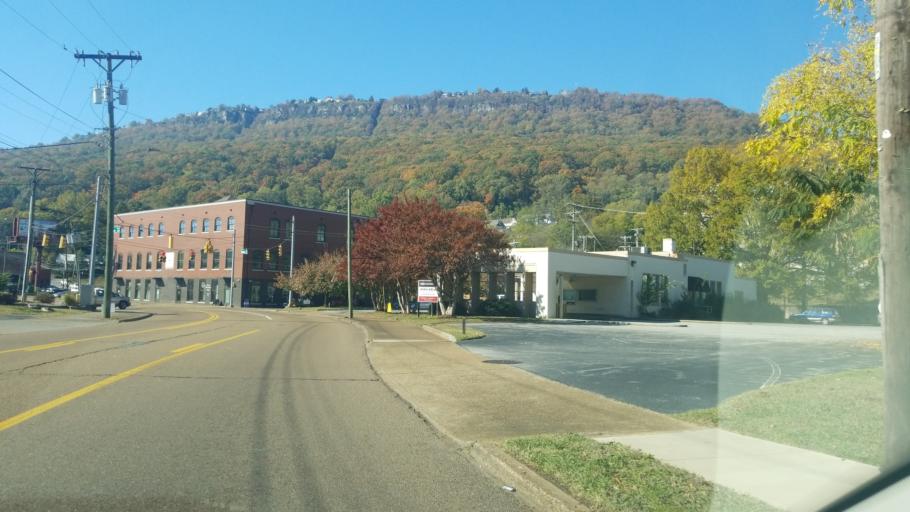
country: US
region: Tennessee
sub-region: Hamilton County
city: Lookout Mountain
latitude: 35.0115
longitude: -85.3270
